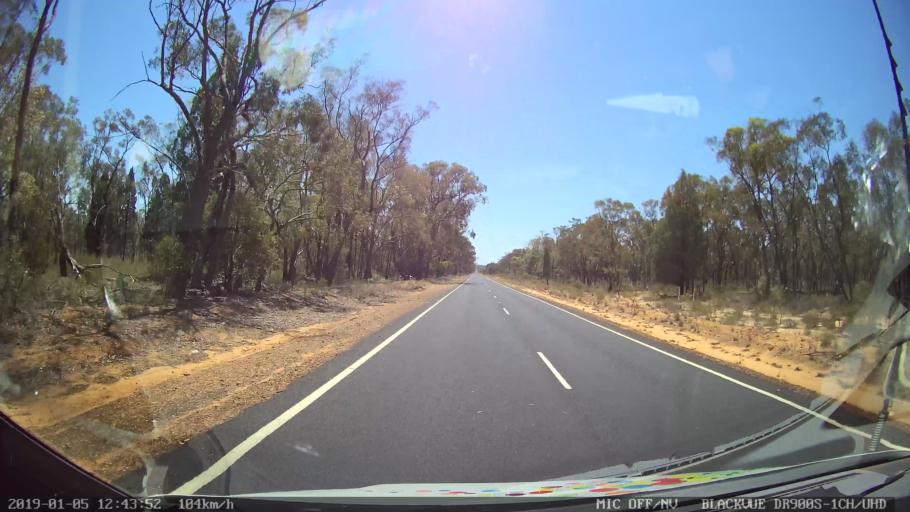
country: AU
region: New South Wales
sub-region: Warrumbungle Shire
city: Coonabarabran
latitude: -31.1436
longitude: 149.5298
